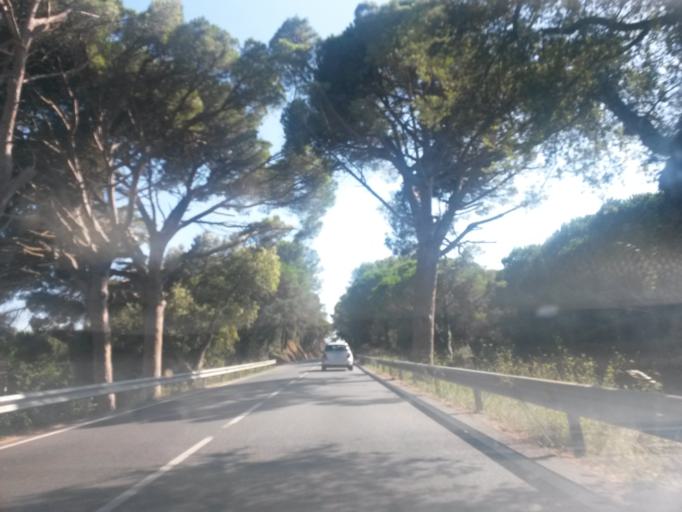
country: ES
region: Catalonia
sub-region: Provincia de Girona
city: Regencos
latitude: 41.9414
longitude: 3.1627
